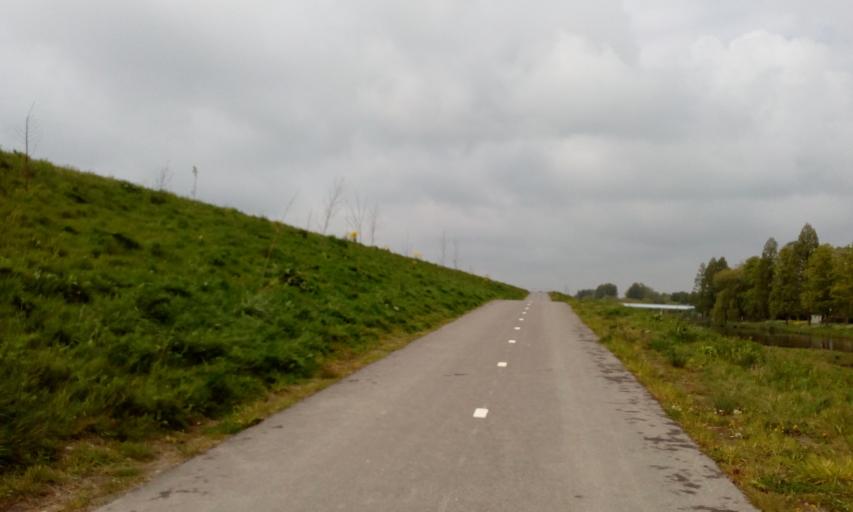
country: NL
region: South Holland
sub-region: Gemeente Schiedam
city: Schiedam
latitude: 51.9328
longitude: 4.3649
